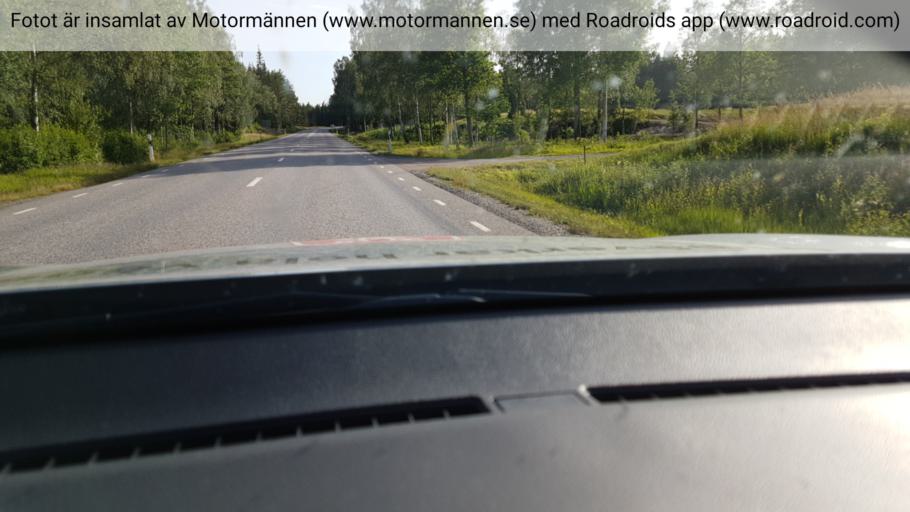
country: SE
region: Joenkoeping
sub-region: Varnamo Kommun
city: Bor
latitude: 57.2722
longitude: 14.2354
